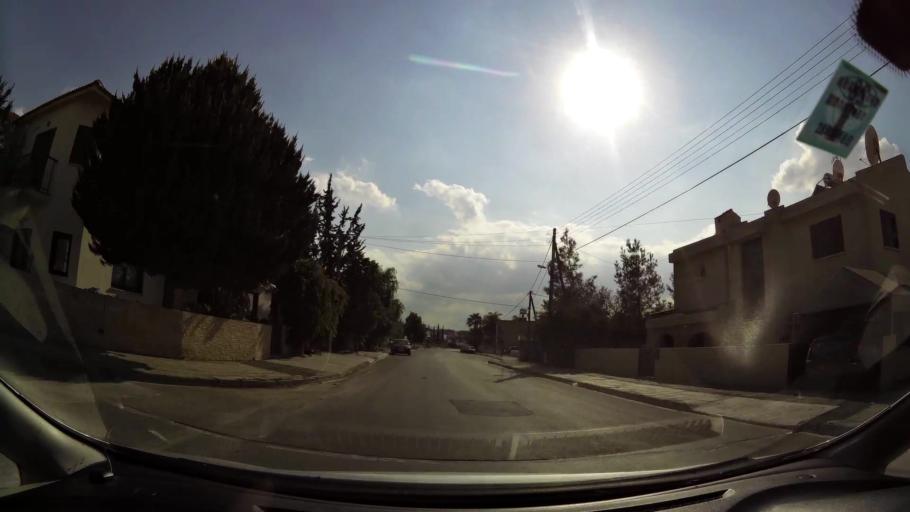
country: CY
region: Lefkosia
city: Kato Deftera
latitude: 35.1467
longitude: 33.2999
